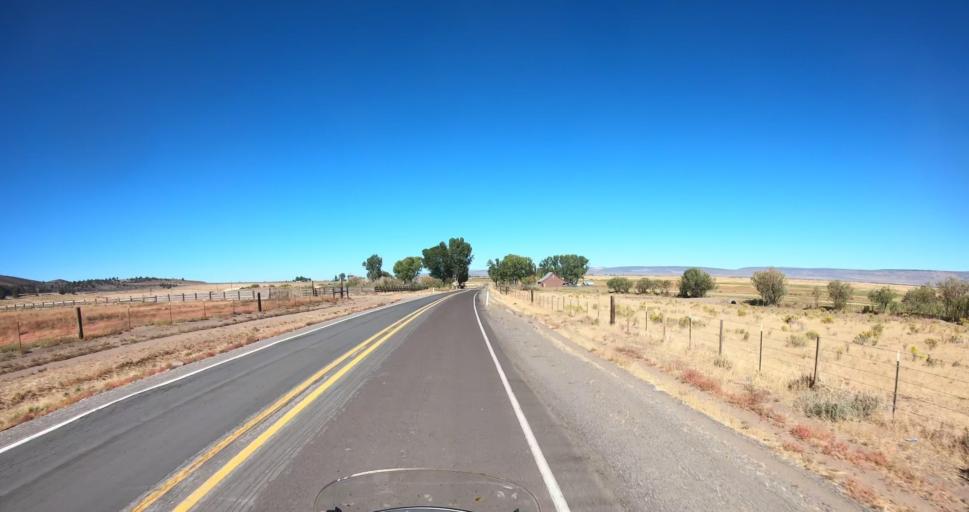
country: US
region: Oregon
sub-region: Lake County
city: Lakeview
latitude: 42.6565
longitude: -120.5234
